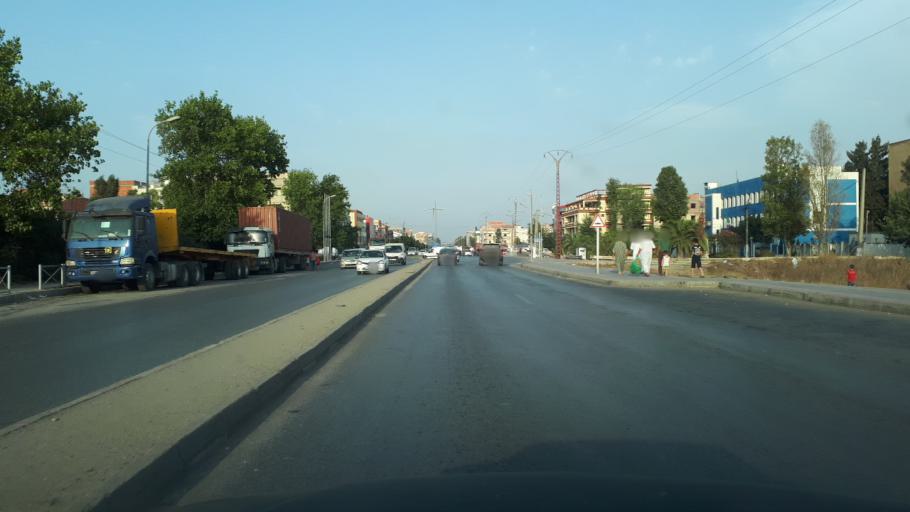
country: DZ
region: Alger
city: Dar el Beida
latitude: 36.7296
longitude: 3.2291
